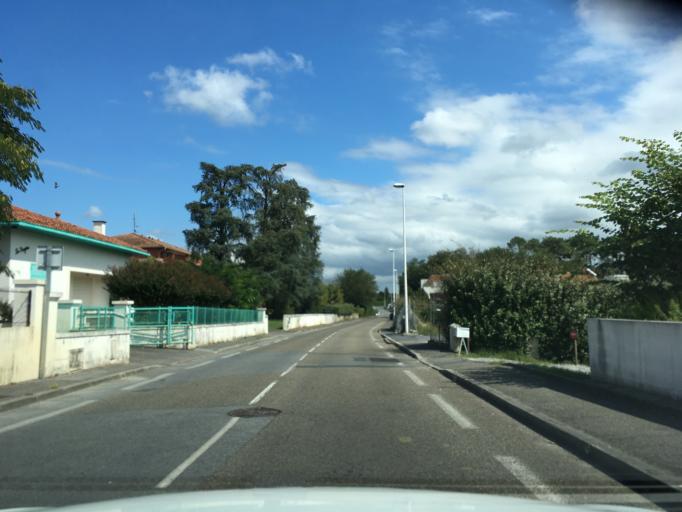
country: FR
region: Aquitaine
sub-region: Departement des Pyrenees-Atlantiques
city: Mouguerre
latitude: 43.4943
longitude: -1.4440
